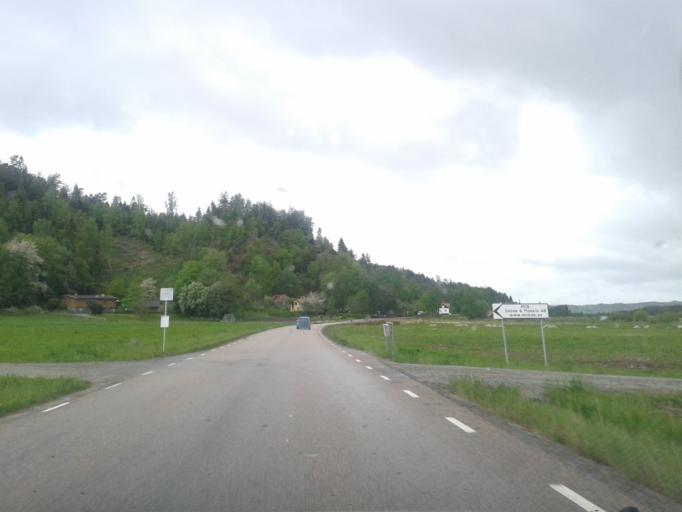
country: SE
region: Vaestra Goetaland
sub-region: Lilla Edets Kommun
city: Lodose
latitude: 58.0042
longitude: 12.1253
